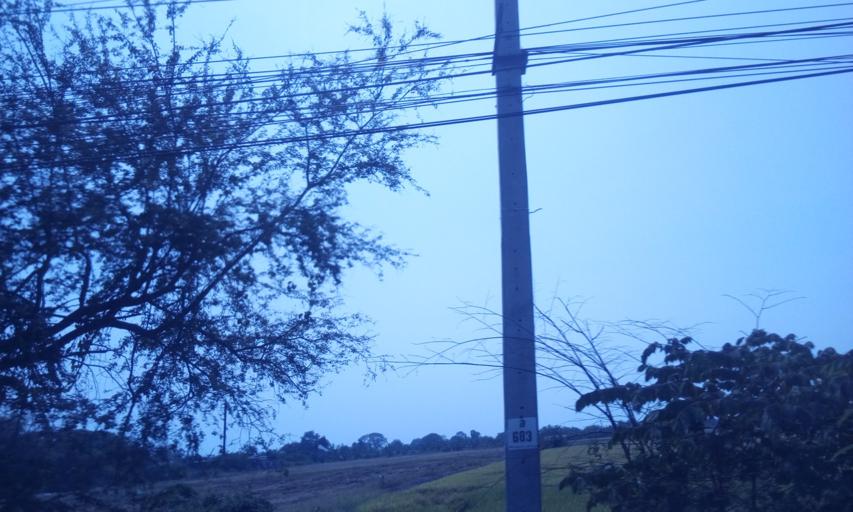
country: TH
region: Nonthaburi
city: Sai Noi
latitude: 13.9467
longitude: 100.3140
